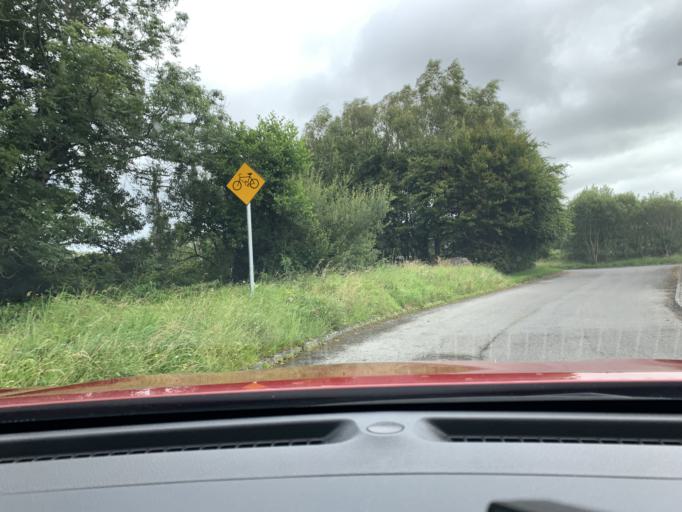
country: IE
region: Connaught
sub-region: Roscommon
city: Boyle
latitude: 53.9840
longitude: -8.2807
